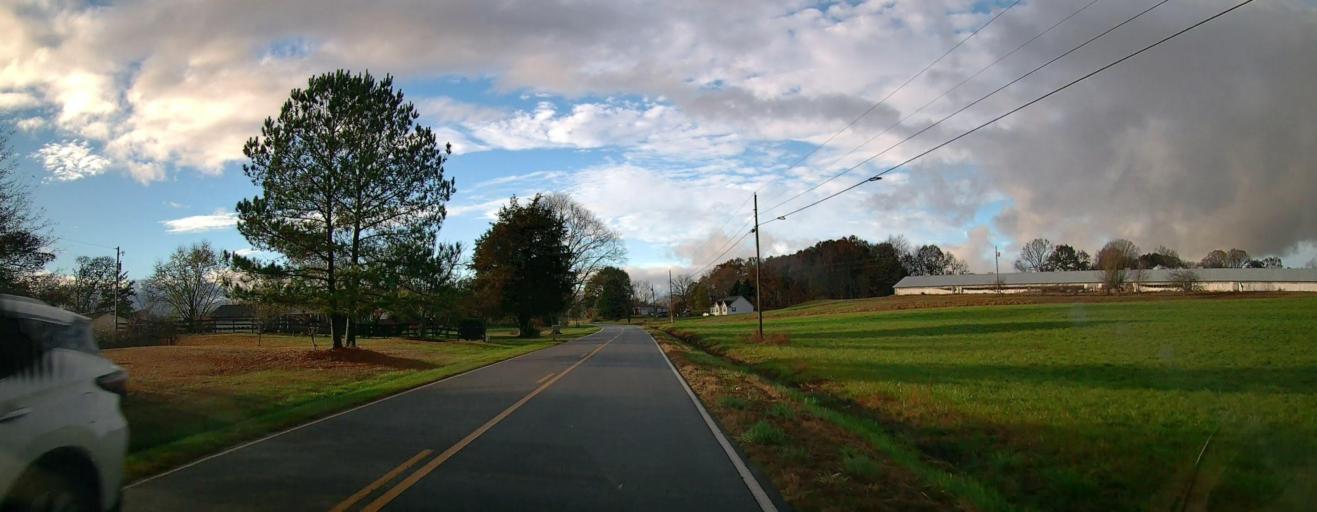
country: US
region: Georgia
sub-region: White County
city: Cleveland
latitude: 34.5347
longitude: -83.6755
